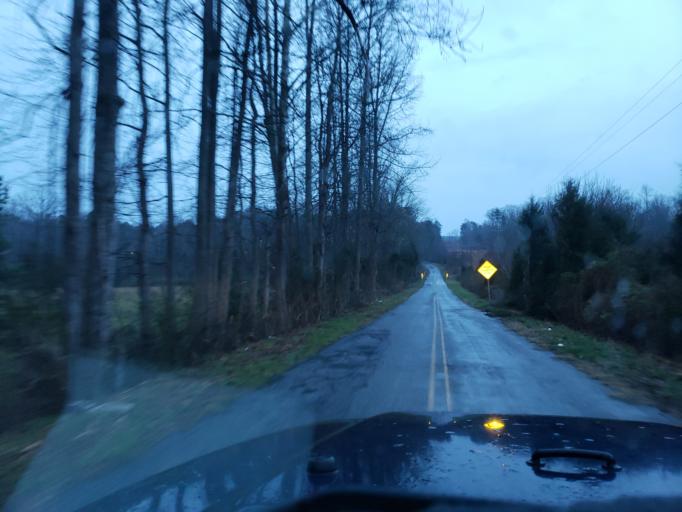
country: US
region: North Carolina
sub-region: Cleveland County
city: White Plains
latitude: 35.1468
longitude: -81.4109
